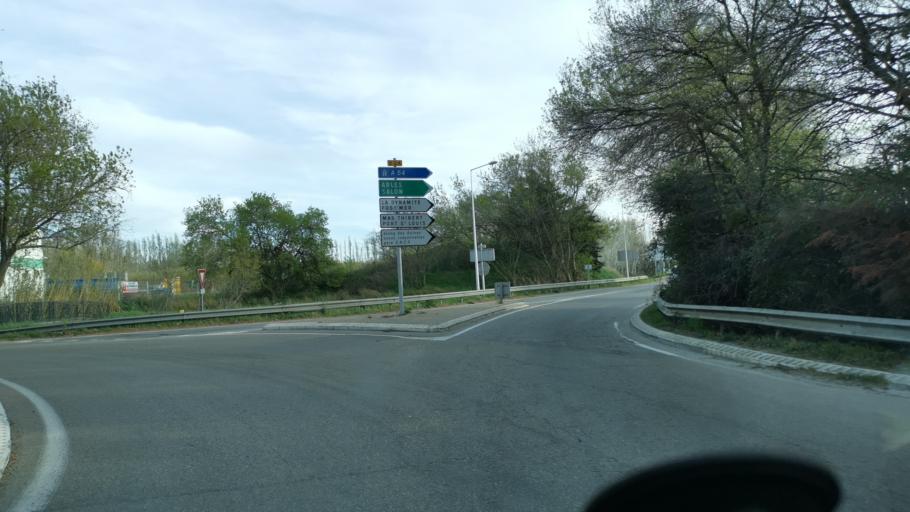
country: FR
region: Provence-Alpes-Cote d'Azur
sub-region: Departement des Bouches-du-Rhone
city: Saint-Martin-de-Crau
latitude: 43.6319
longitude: 4.8065
